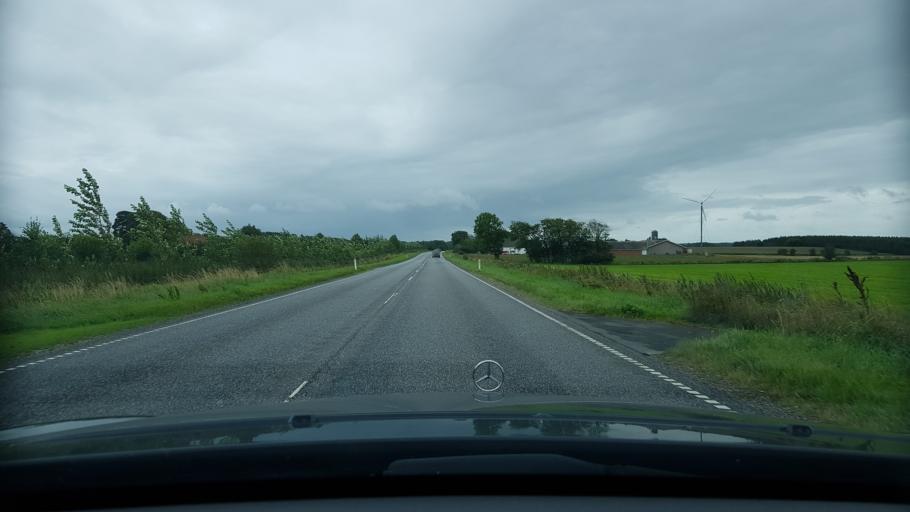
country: DK
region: Central Jutland
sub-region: Randers Kommune
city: Spentrup
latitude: 56.5514
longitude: 10.1036
